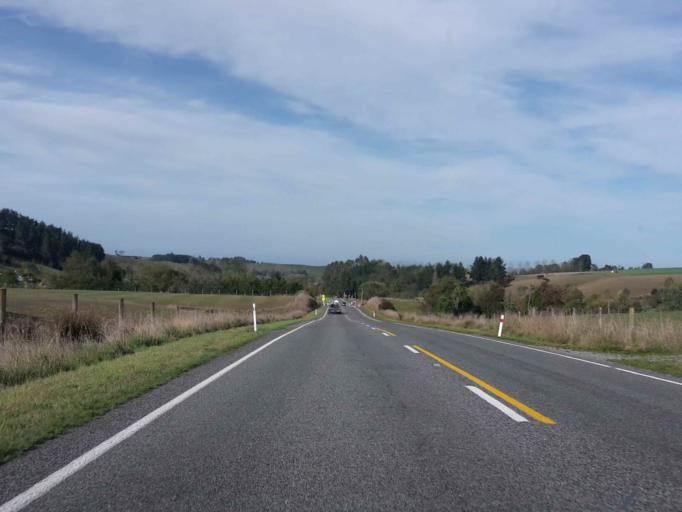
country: NZ
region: Canterbury
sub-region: Timaru District
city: Pleasant Point
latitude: -44.1114
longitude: 171.1385
